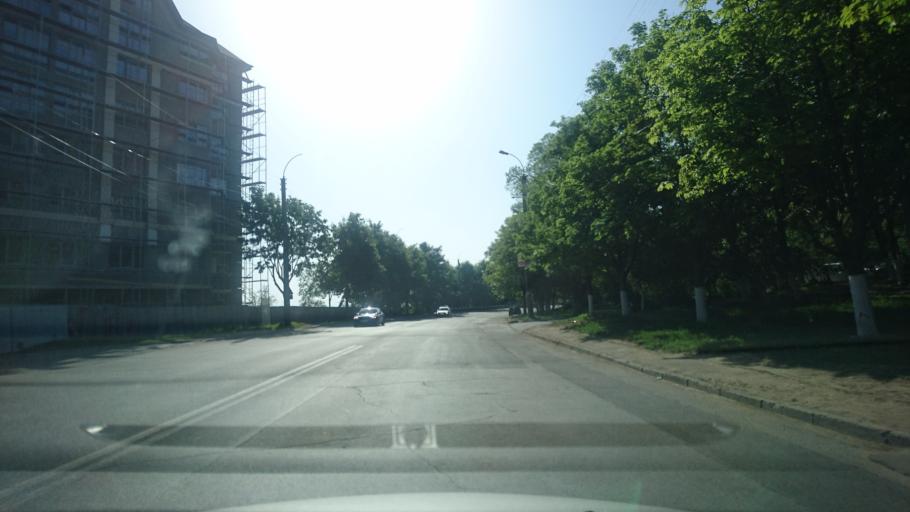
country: MD
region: Chisinau
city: Vatra
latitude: 47.0469
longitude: 28.7674
